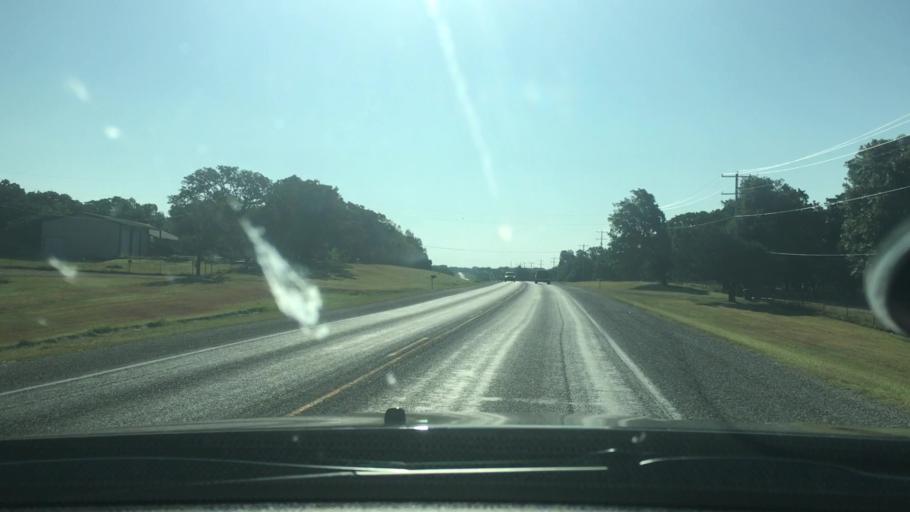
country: US
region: Oklahoma
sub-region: Johnston County
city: Tishomingo
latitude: 34.2369
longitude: -96.7279
